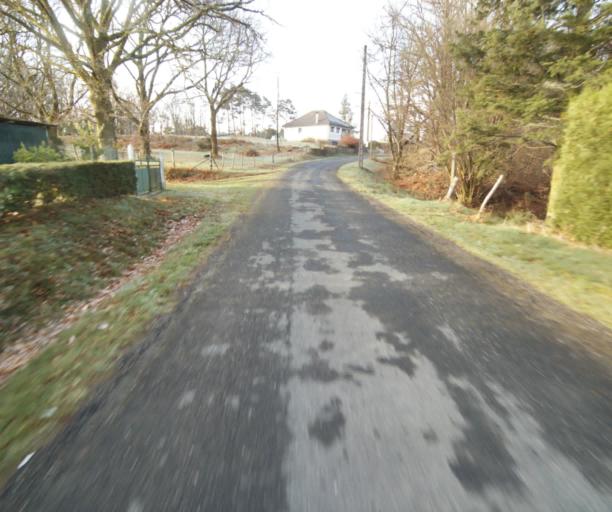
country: FR
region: Limousin
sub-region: Departement de la Correze
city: Correze
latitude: 45.3260
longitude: 1.8664
